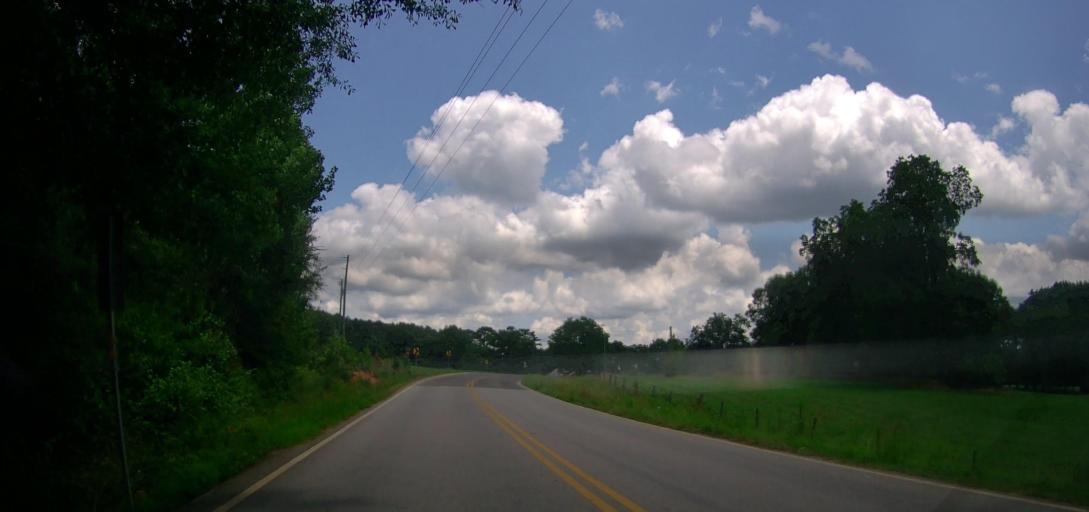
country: US
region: Georgia
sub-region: Troup County
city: Hogansville
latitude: 33.1578
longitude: -84.8584
